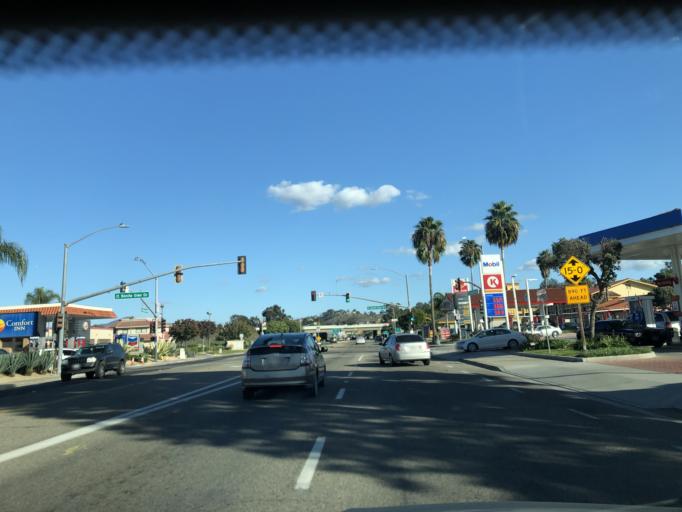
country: US
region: California
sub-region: San Diego County
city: Chula Vista
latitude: 32.6480
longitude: -117.0648
